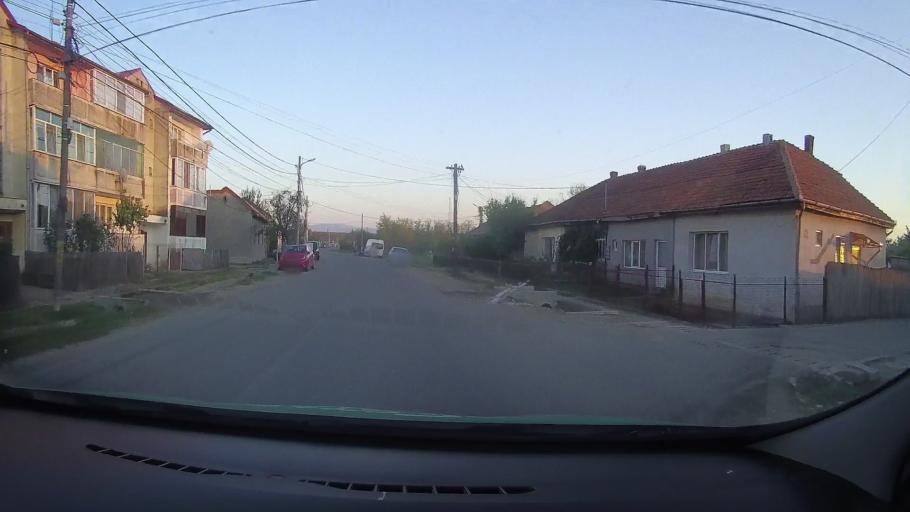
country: RO
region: Timis
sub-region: Comuna Manastiur
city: Manastiur
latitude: 45.8296
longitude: 22.0667
